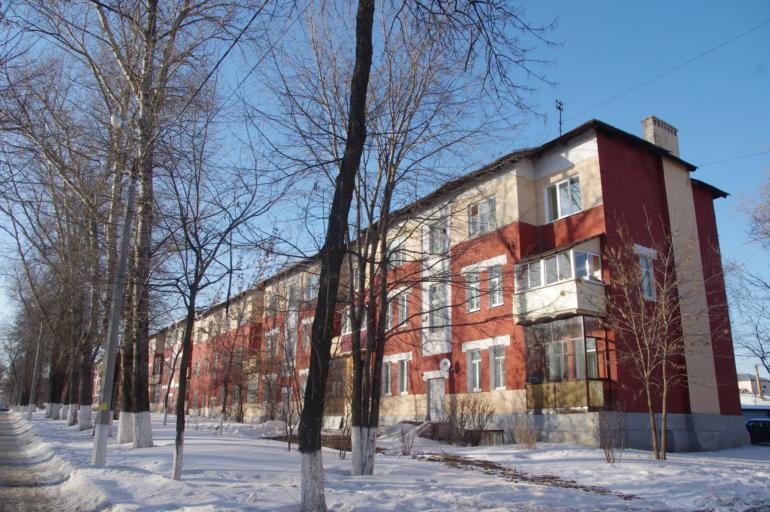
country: RU
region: Moskovskaya
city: Kolomna
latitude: 55.0909
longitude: 38.7806
